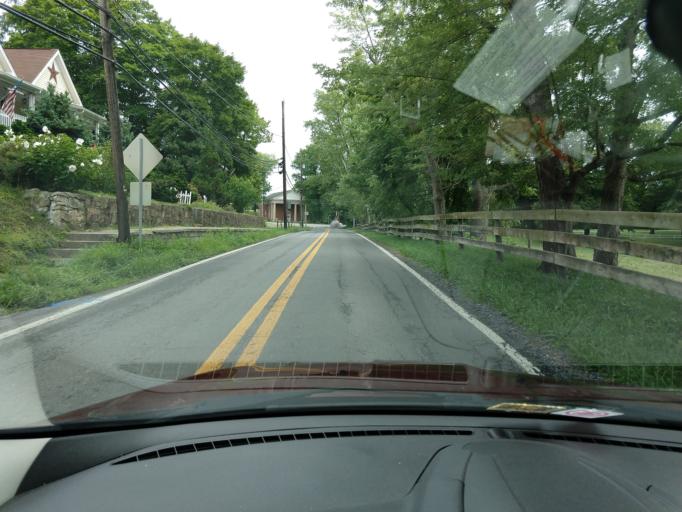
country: US
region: West Virginia
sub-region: Fayette County
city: Oak Hill
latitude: 37.9709
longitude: -81.1511
